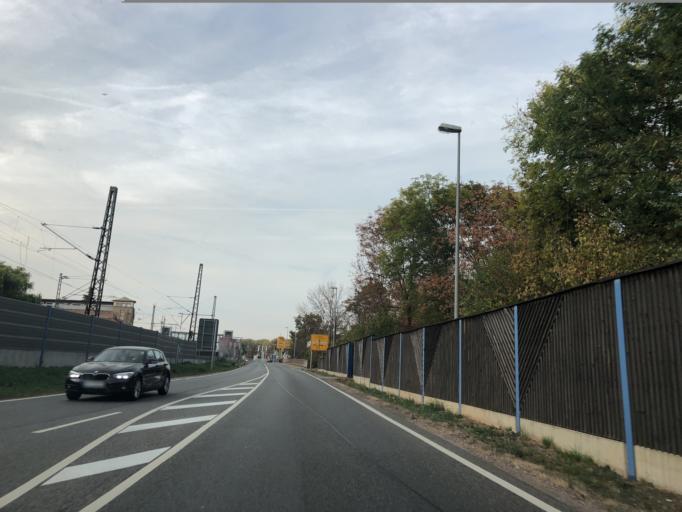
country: DE
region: Rheinland-Pfalz
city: Oppenheim
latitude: 49.8546
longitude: 8.3599
